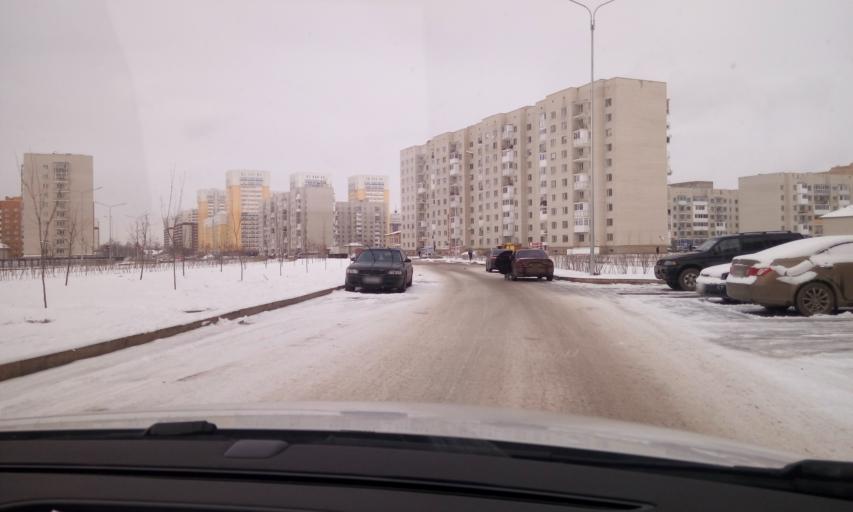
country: KZ
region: Astana Qalasy
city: Astana
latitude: 51.1243
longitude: 71.5051
